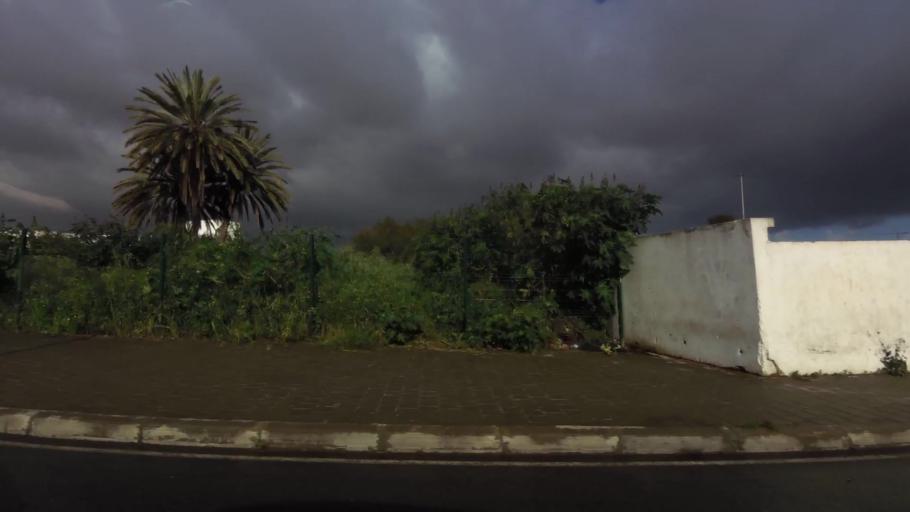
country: MA
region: Grand Casablanca
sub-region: Casablanca
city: Casablanca
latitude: 33.5503
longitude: -7.6521
